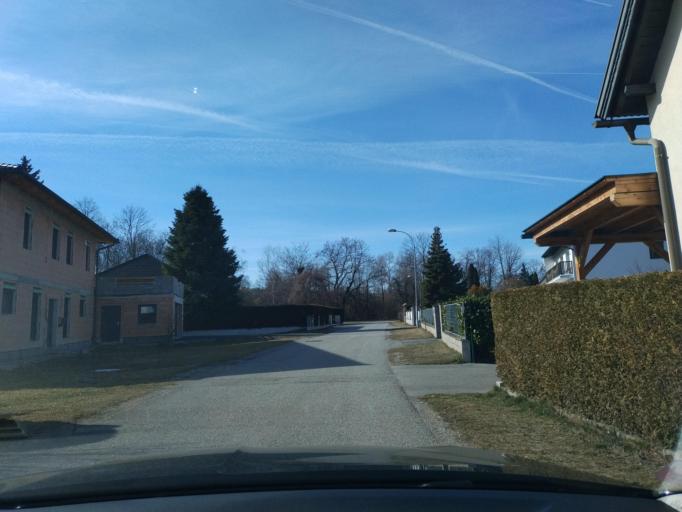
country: AT
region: Lower Austria
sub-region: Politischer Bezirk Neunkirchen
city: Pitten
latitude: 47.7326
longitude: 16.1767
